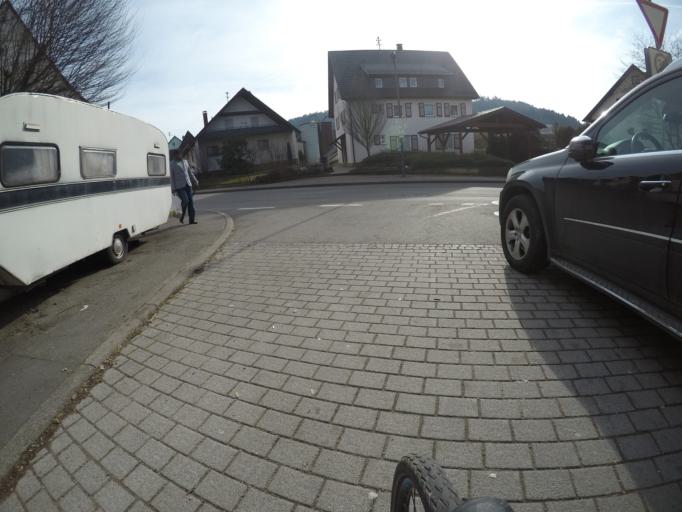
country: DE
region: Baden-Wuerttemberg
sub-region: Karlsruhe Region
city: Wildberg
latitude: 48.6504
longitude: 8.7749
